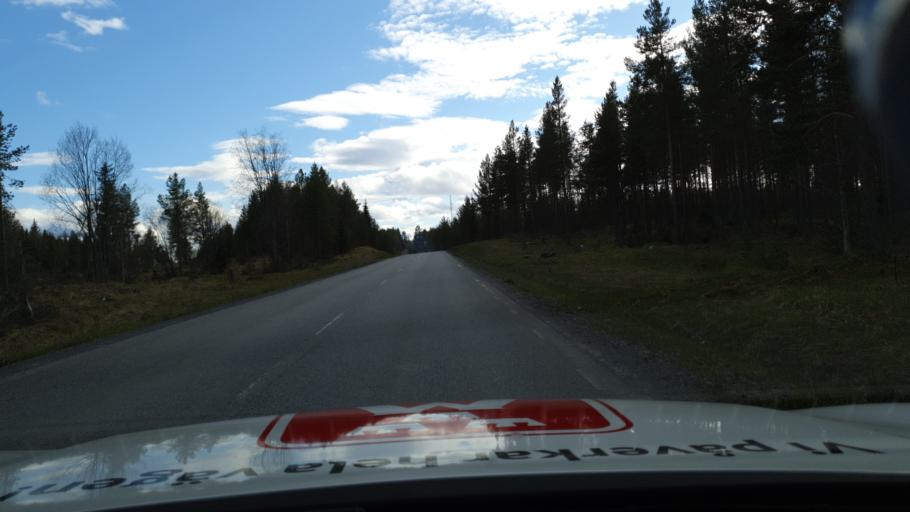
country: SE
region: Jaemtland
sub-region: Krokoms Kommun
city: Krokom
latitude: 63.2583
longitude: 14.4325
